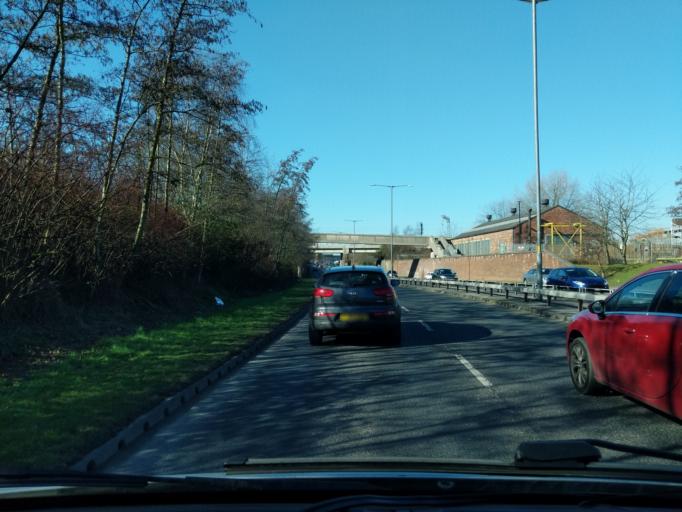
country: GB
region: England
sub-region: St. Helens
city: St Helens
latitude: 53.4482
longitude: -2.7341
